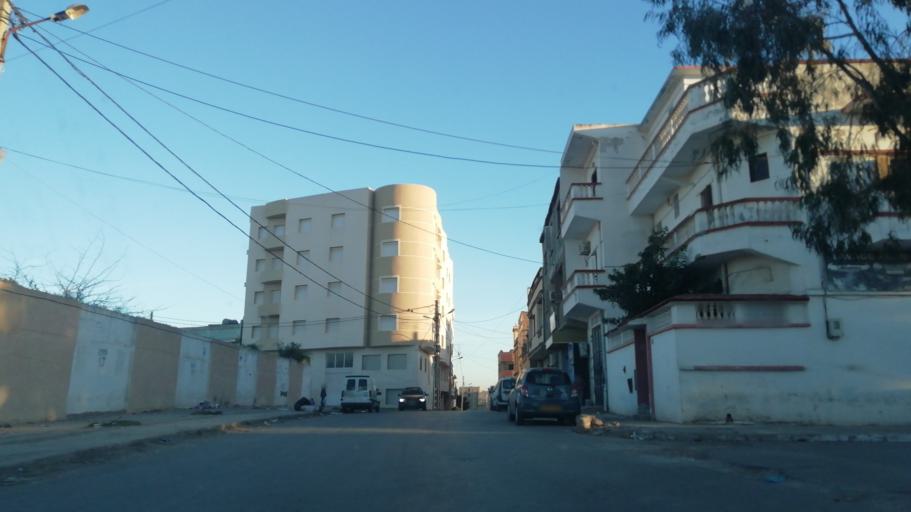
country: DZ
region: Oran
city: Bir el Djir
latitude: 35.7268
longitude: -0.5774
